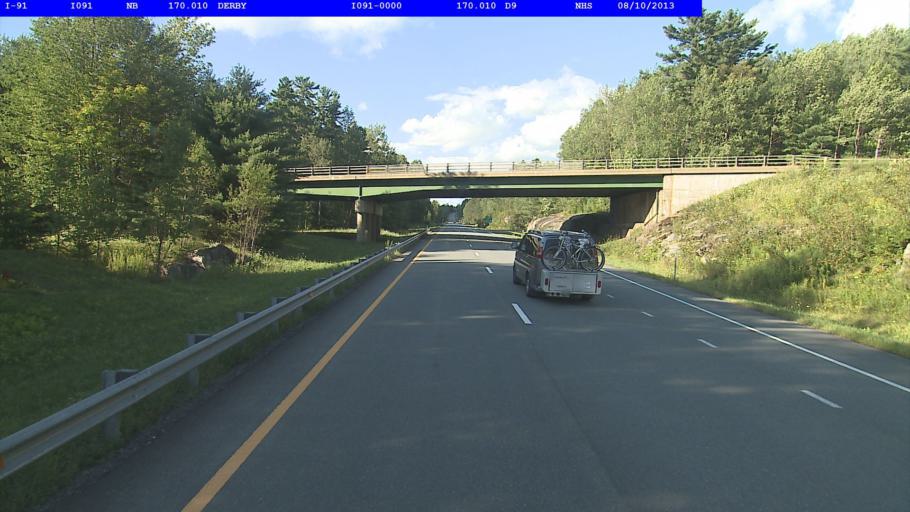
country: US
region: Vermont
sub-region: Orleans County
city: Newport
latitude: 44.9219
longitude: -72.1729
